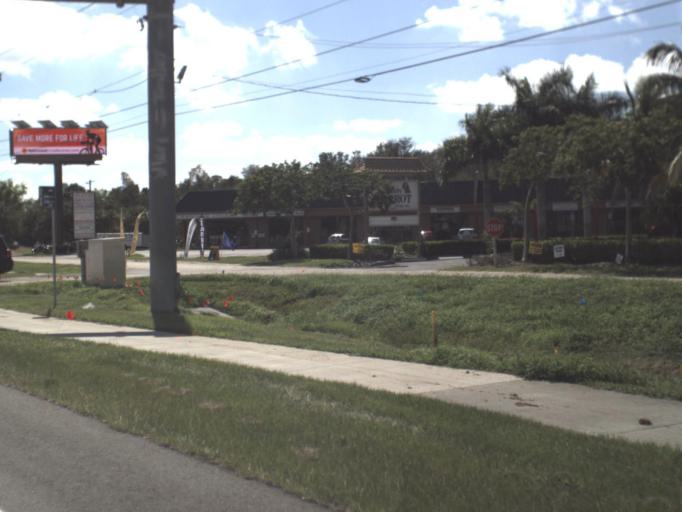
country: US
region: Florida
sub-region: Lee County
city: San Carlos Park
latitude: 26.4907
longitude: -81.8444
